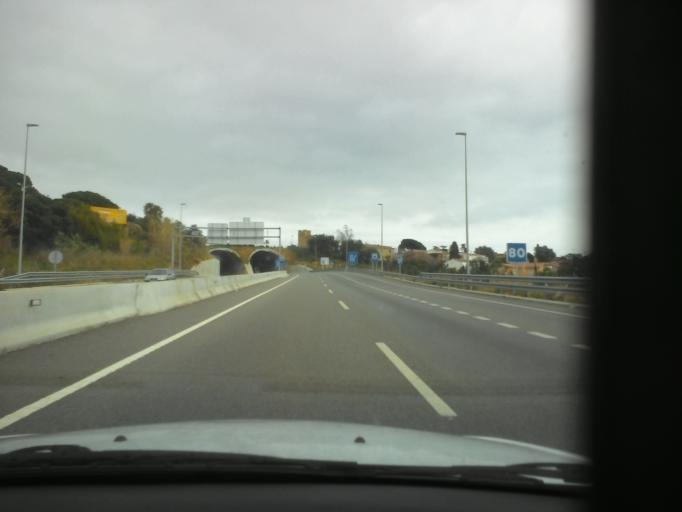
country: ES
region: Catalonia
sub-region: Provincia de Girona
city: Castell-Platja d'Aro
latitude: 41.8218
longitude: 3.0564
